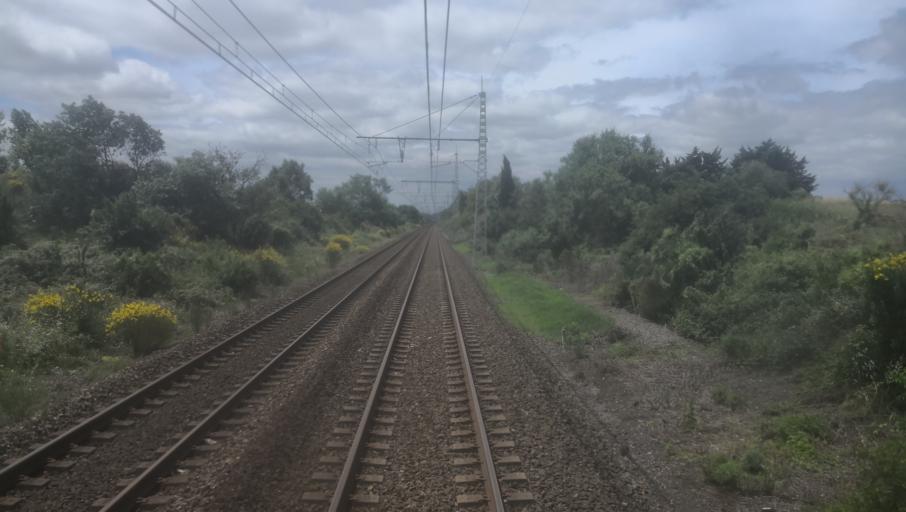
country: FR
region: Languedoc-Roussillon
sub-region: Departement de l'Aude
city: Carcassonne
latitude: 43.2196
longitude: 2.3777
